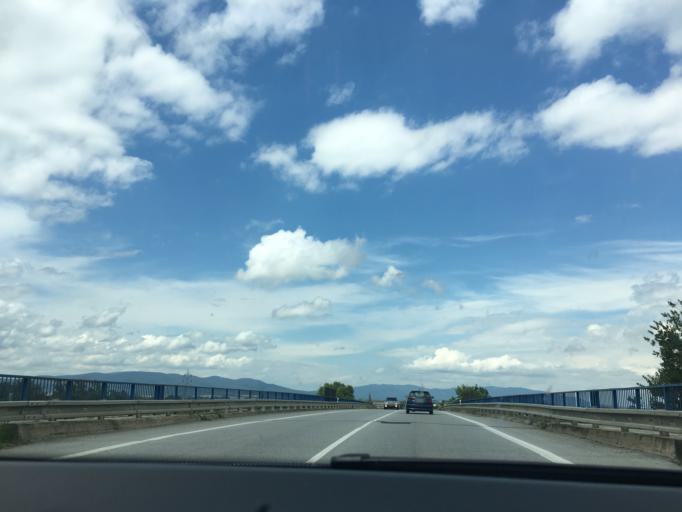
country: SK
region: Kosicky
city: Trebisov
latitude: 48.6251
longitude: 21.6980
